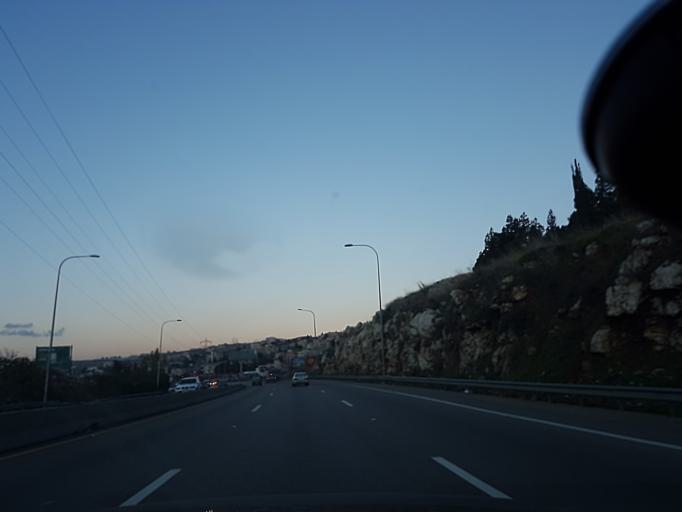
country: LB
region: Liban-Sud
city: Sidon
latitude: 33.6536
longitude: 35.4216
